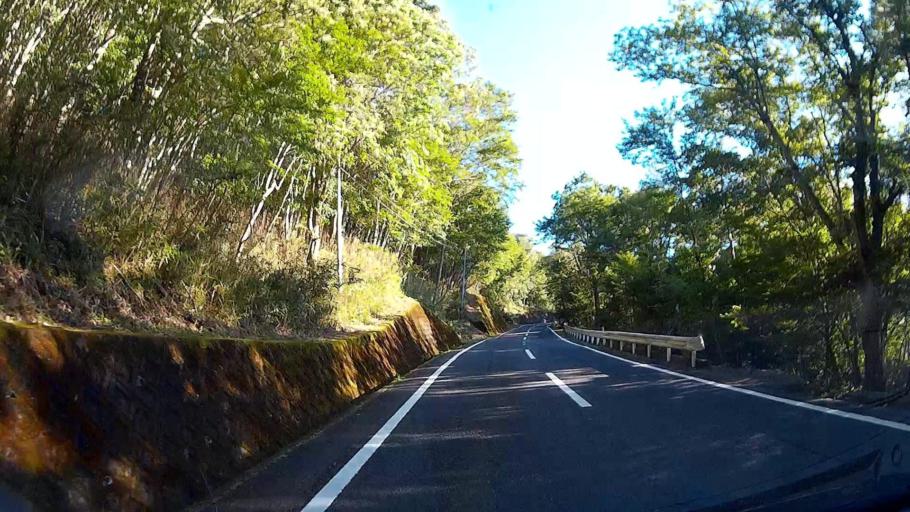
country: JP
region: Shizuoka
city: Shizuoka-shi
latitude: 35.1886
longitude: 138.2493
